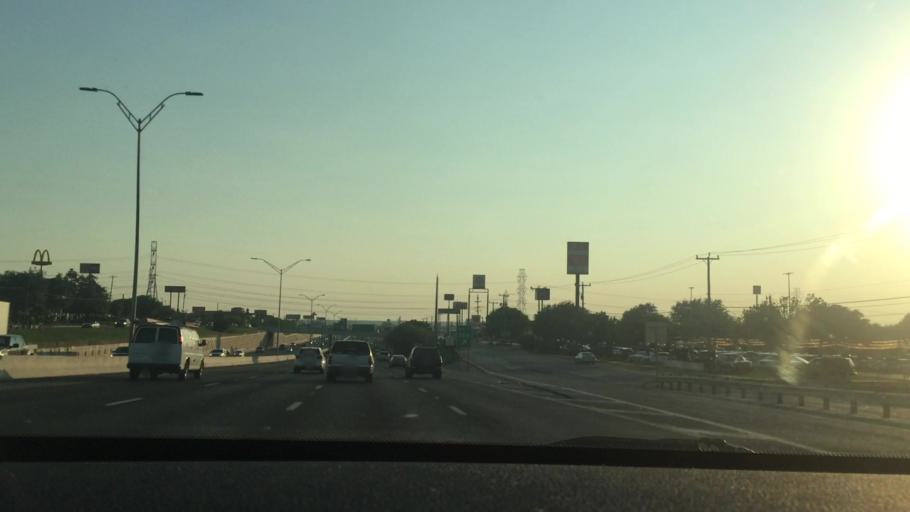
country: US
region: Texas
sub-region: Bexar County
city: Live Oak
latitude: 29.5476
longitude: -98.3659
